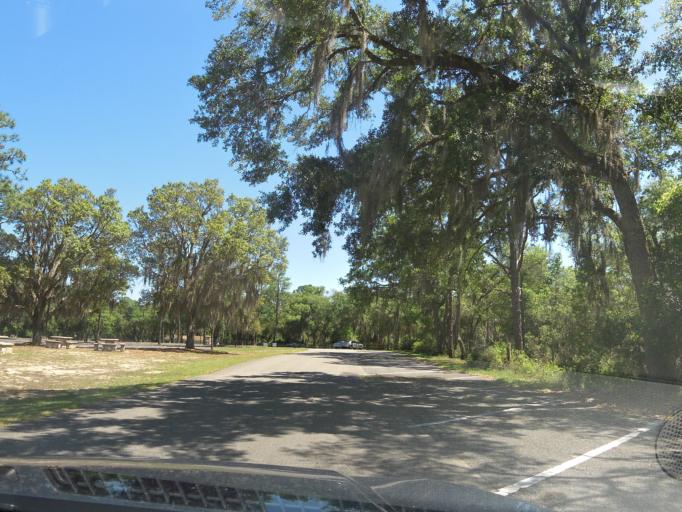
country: US
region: Florida
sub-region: Clay County
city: Keystone Heights
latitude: 29.8281
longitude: -81.9540
